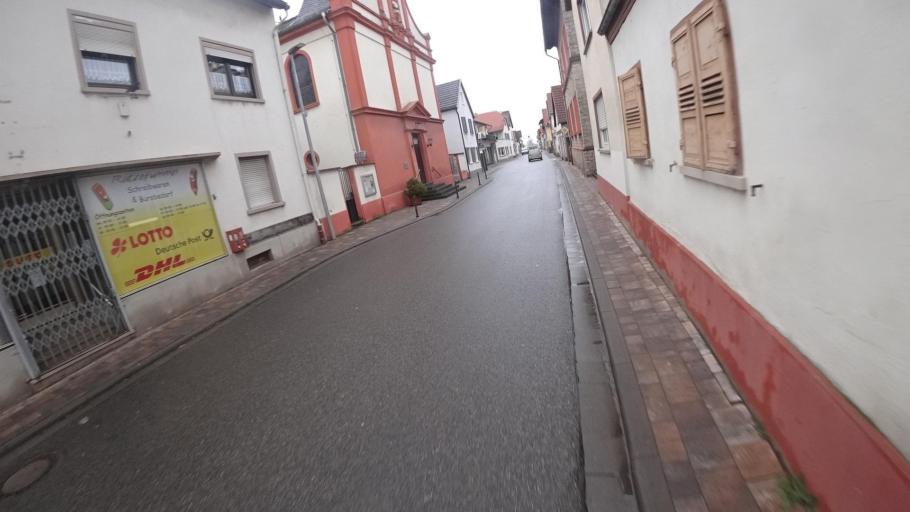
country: DE
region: Rheinland-Pfalz
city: Gimbsheim
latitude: 49.7798
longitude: 8.3752
